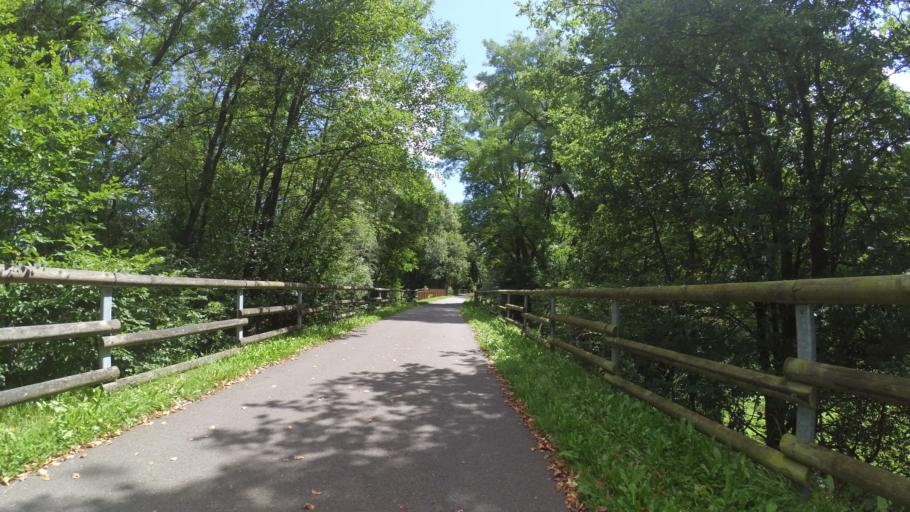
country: DE
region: Saarland
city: Sankt Wendel
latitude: 49.4852
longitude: 7.1544
